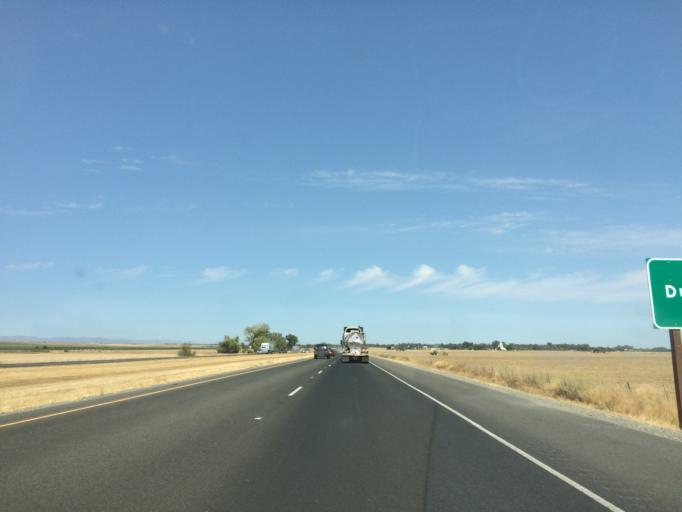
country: US
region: California
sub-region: Yolo County
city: Dunnigan
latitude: 38.8667
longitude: -121.9592
